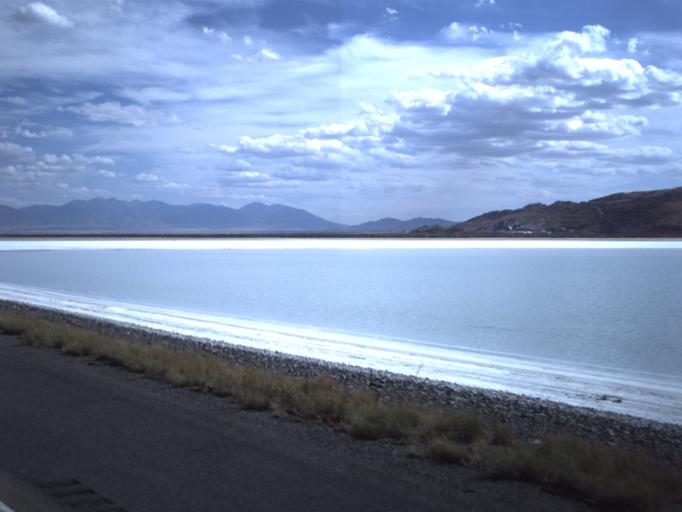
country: US
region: Utah
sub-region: Tooele County
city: Grantsville
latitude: 40.7299
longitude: -112.5890
